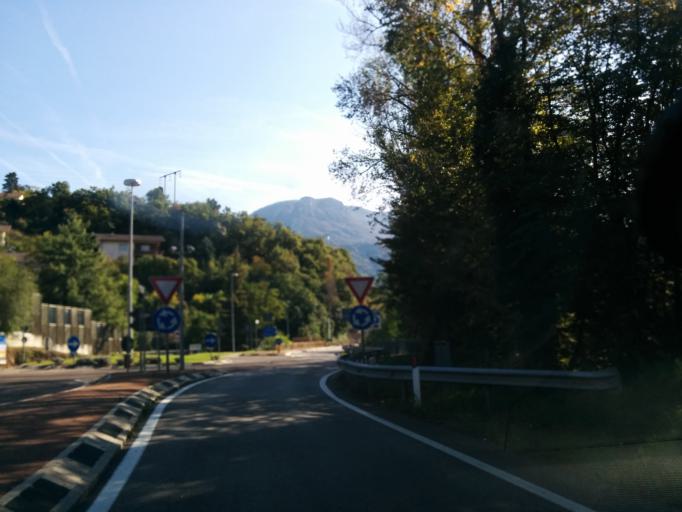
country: IT
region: Trentino-Alto Adige
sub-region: Provincia di Trento
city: Povo
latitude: 46.0738
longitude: 11.1386
